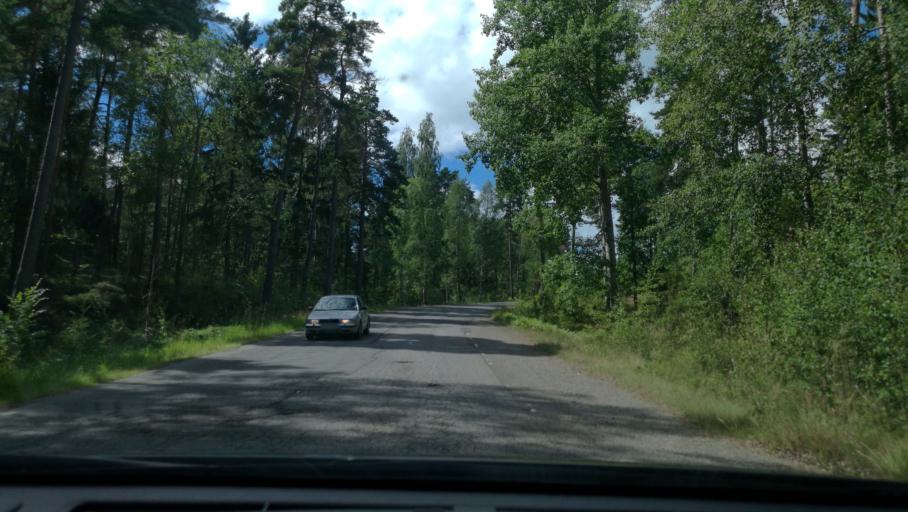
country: SE
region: OEstergoetland
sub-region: Norrkopings Kommun
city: Krokek
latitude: 58.6603
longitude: 16.4637
